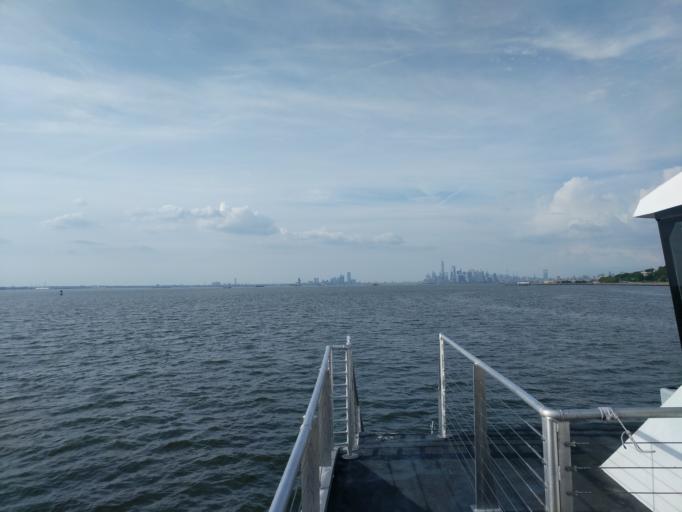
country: US
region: New York
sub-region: Kings County
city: Bensonhurst
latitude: 40.6298
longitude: -74.0439
